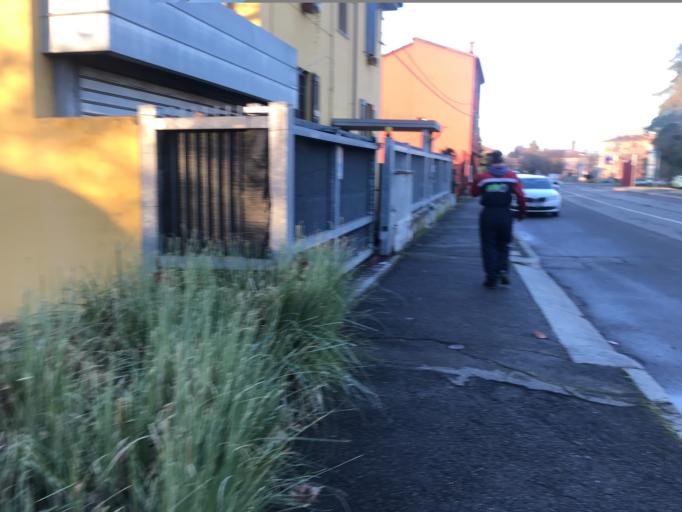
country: IT
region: Emilia-Romagna
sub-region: Provincia di Bologna
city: Progresso
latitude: 44.5406
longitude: 11.3513
